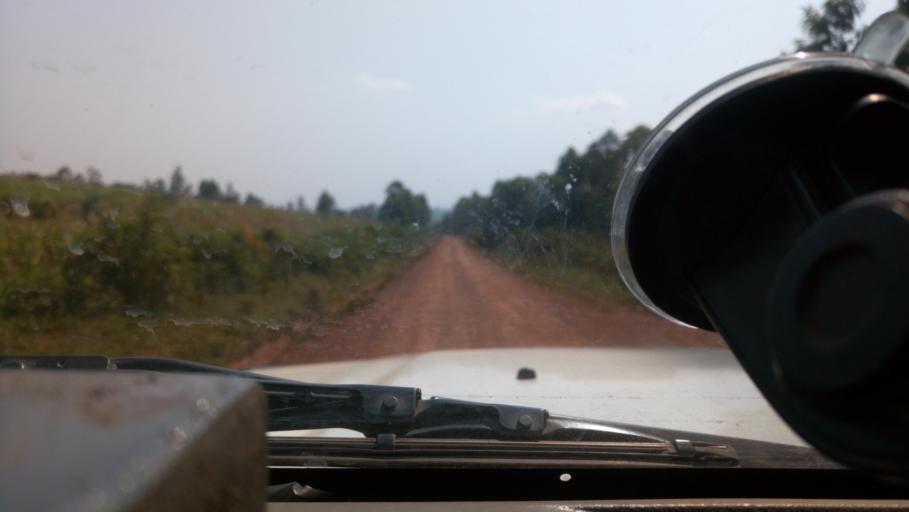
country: KE
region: Kisii
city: Ogembo
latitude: -0.8839
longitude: 34.6137
